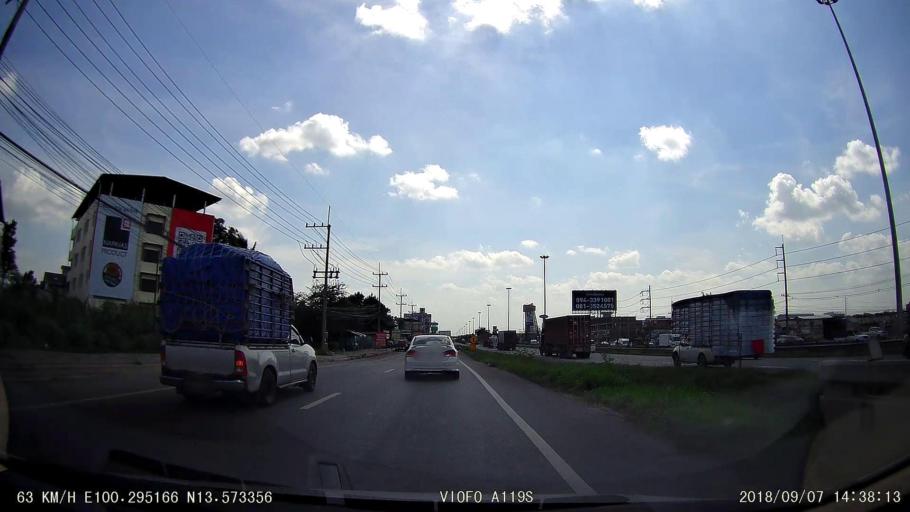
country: TH
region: Samut Sakhon
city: Samut Sakhon
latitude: 13.5731
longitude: 100.2953
